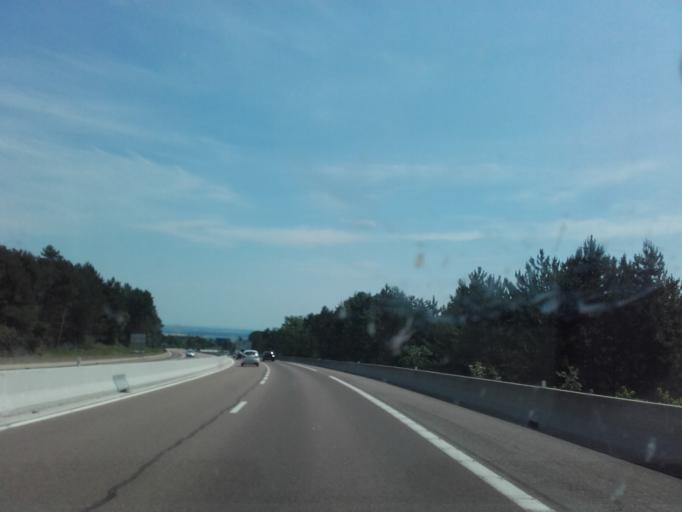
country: FR
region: Bourgogne
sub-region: Departement de la Cote-d'Or
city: Savigny-les-Beaune
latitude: 47.0572
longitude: 4.7852
